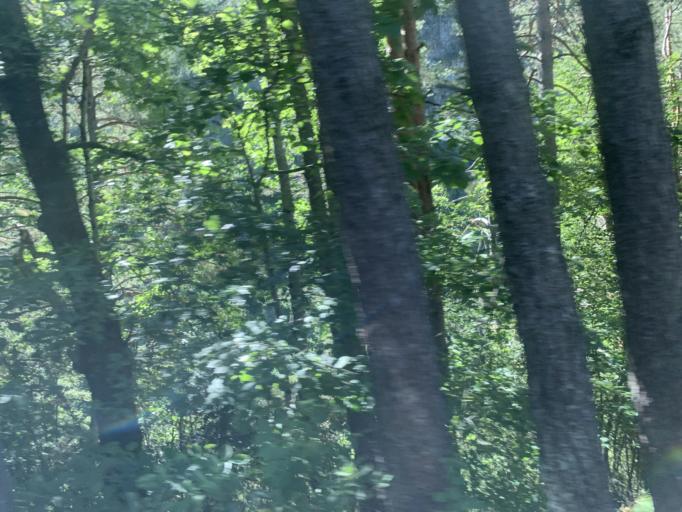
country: ES
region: Aragon
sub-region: Provincia de Huesca
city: Broto
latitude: 42.6527
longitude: -0.0953
